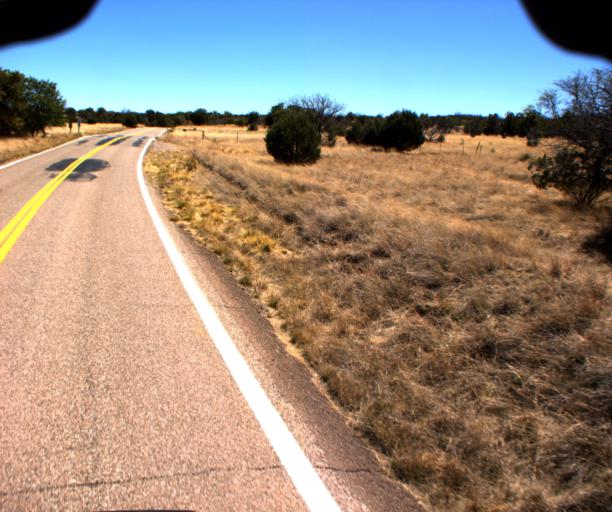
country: US
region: Arizona
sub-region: Cochise County
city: Huachuca City
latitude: 31.5576
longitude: -110.5519
